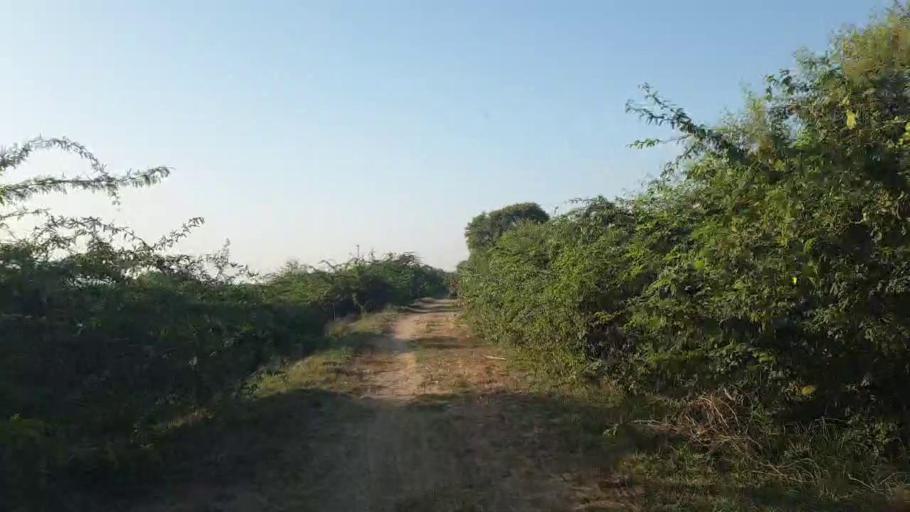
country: PK
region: Sindh
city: Badin
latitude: 24.6115
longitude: 68.7841
